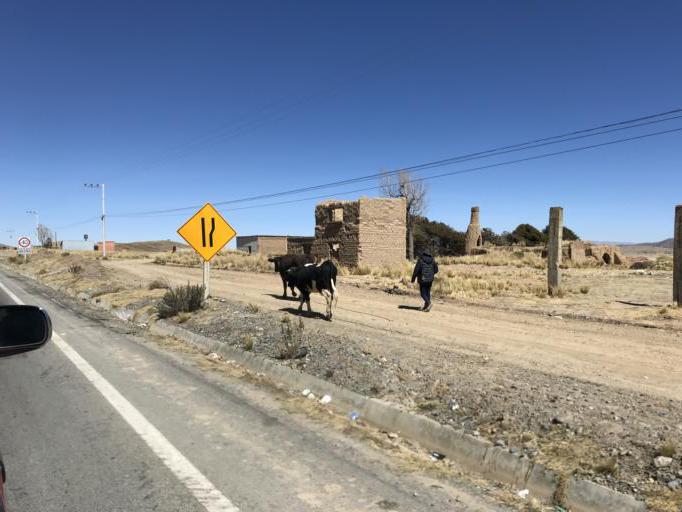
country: BO
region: La Paz
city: Batallas
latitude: -16.2596
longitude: -68.5612
